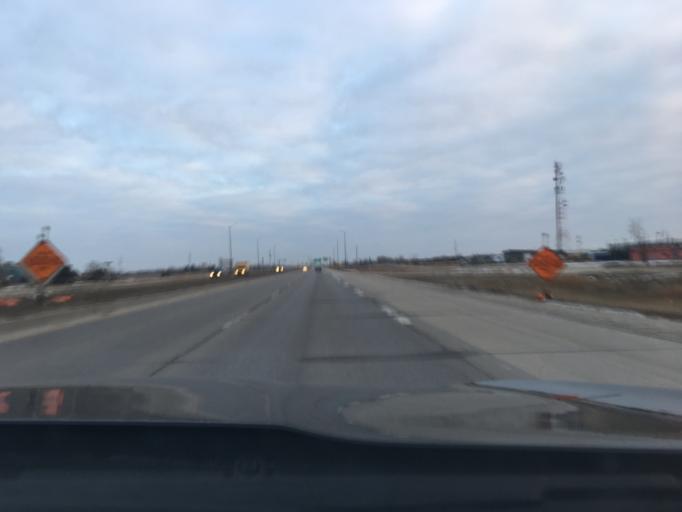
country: CA
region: Manitoba
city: Winnipeg
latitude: 49.9772
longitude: -97.0855
